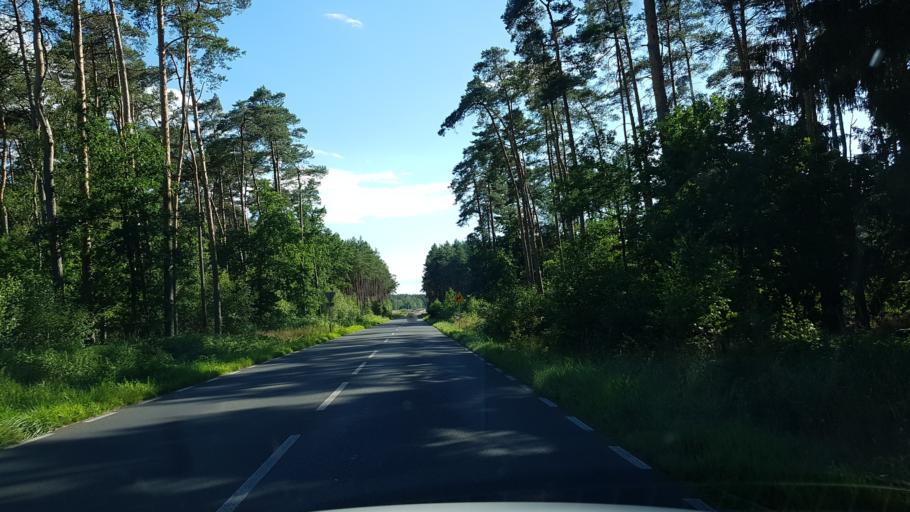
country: PL
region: West Pomeranian Voivodeship
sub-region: Powiat goleniowski
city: Goleniow
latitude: 53.5720
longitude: 14.7892
